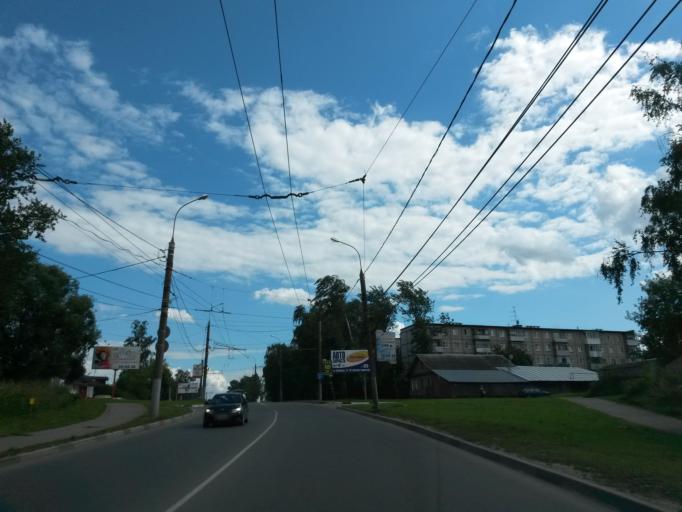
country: RU
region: Ivanovo
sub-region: Gorod Ivanovo
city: Ivanovo
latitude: 56.9829
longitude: 40.9949
